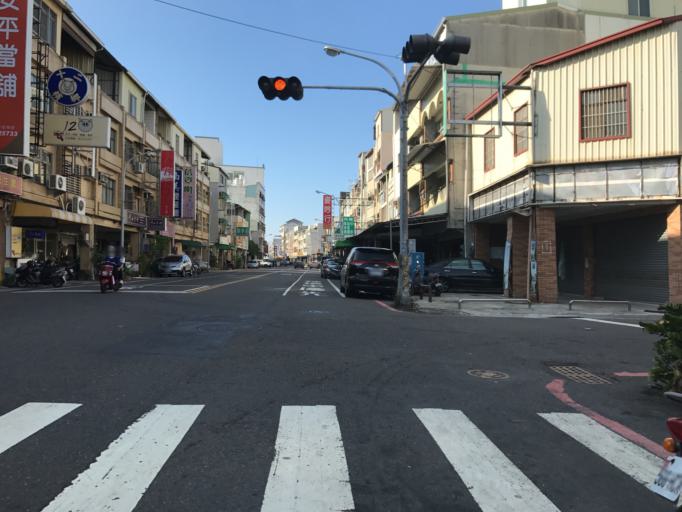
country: TW
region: Taiwan
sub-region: Tainan
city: Tainan
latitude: 22.9994
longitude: 120.1679
